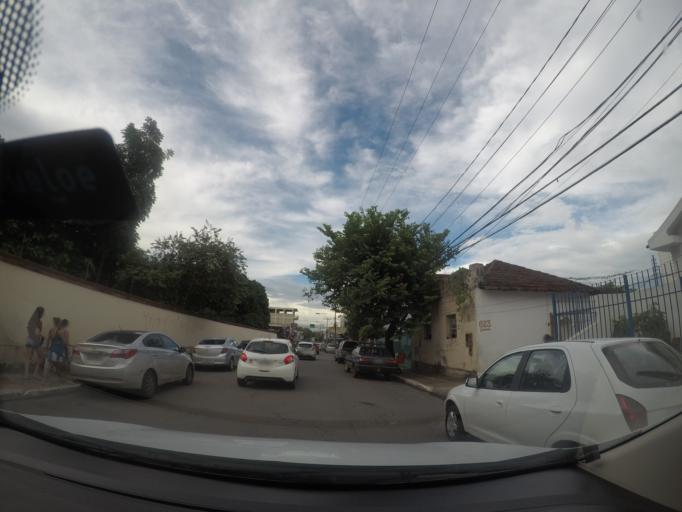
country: BR
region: Goias
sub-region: Goiania
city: Goiania
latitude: -16.6654
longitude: -49.2933
